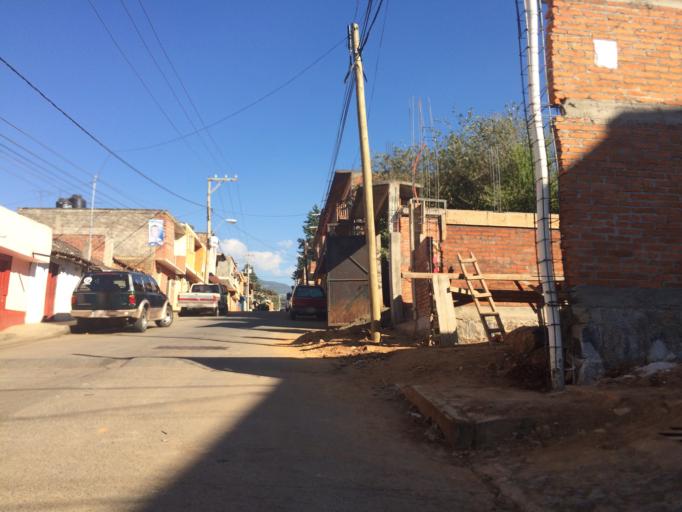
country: MX
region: Michoacan
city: Patzcuaro
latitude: 19.5108
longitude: -101.6011
